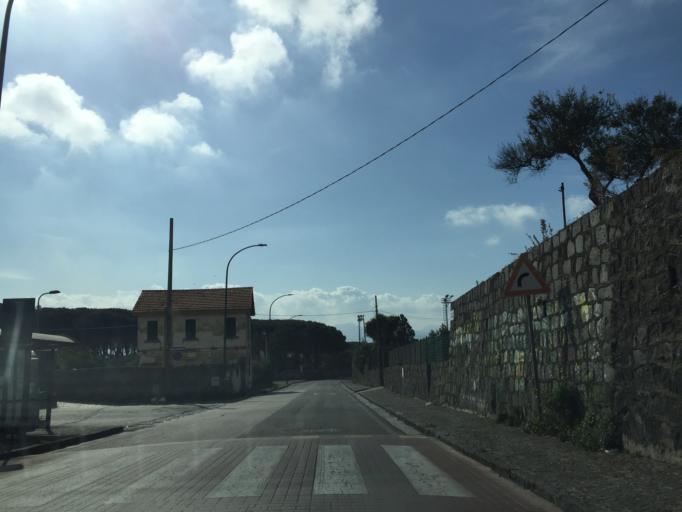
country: IT
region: Campania
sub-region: Provincia di Napoli
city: Torre del Greco
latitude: 40.7805
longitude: 14.4084
